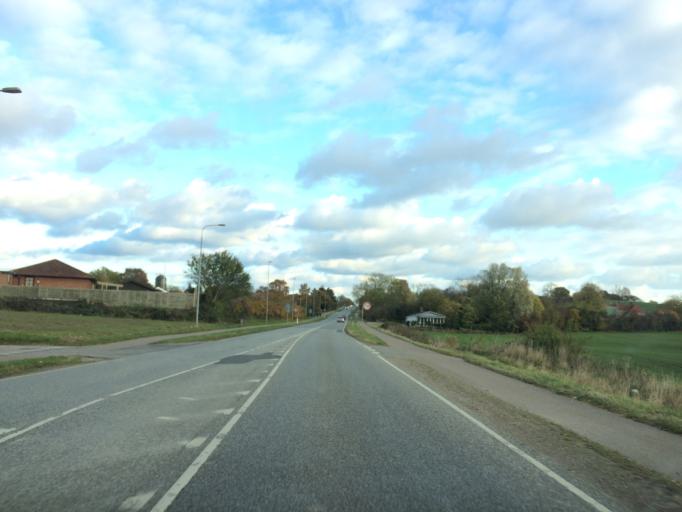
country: DK
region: South Denmark
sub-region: Sonderborg Kommune
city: Nordborg
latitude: 55.0430
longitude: 9.7926
